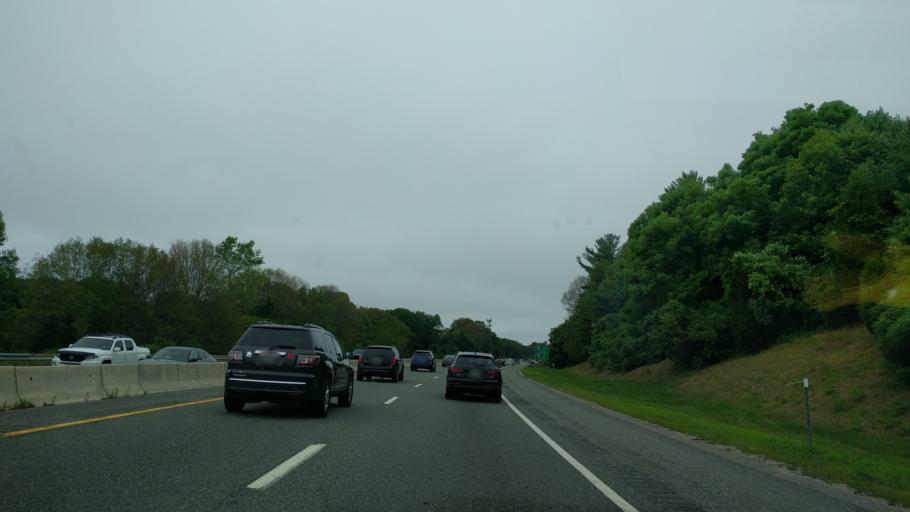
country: US
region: Rhode Island
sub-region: Washington County
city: Exeter
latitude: 41.5935
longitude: -71.4994
